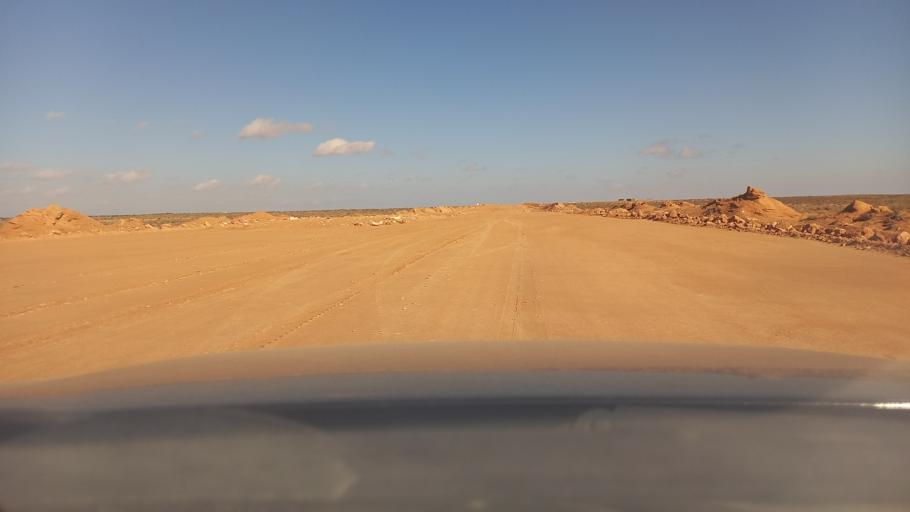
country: TN
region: Madanin
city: Medenine
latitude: 33.2405
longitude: 10.5557
